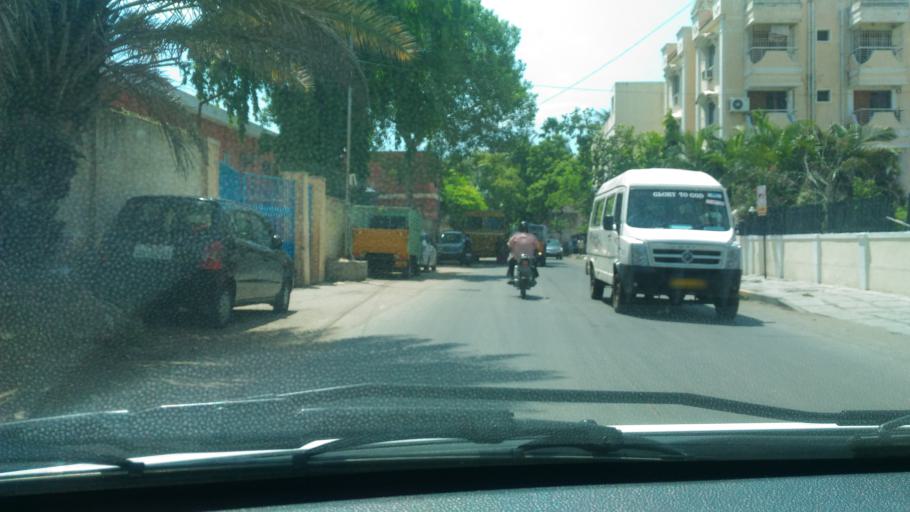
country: IN
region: Tamil Nadu
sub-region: Chennai
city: Chetput
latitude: 13.0513
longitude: 80.2448
